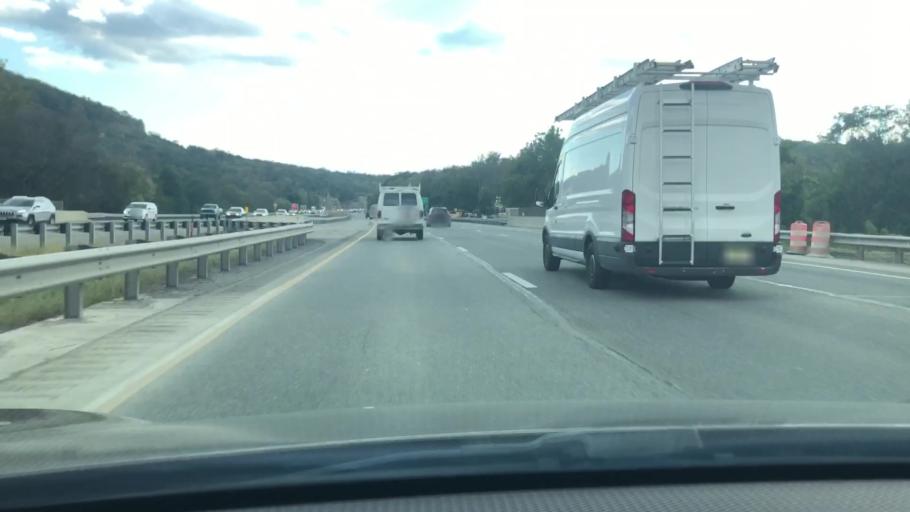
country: US
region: New York
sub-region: Rockland County
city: Sloatsburg
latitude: 41.1938
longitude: -74.1821
